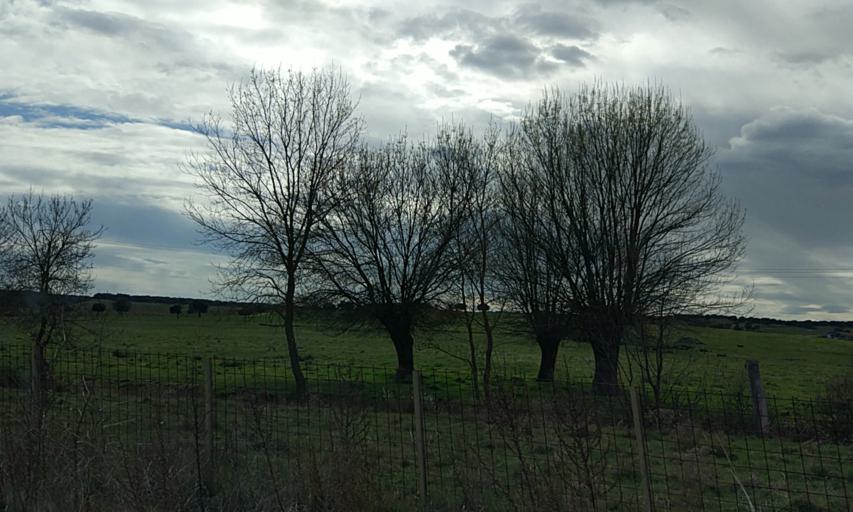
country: ES
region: Castille and Leon
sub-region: Provincia de Salamanca
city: Pastores
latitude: 40.5343
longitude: -6.5666
